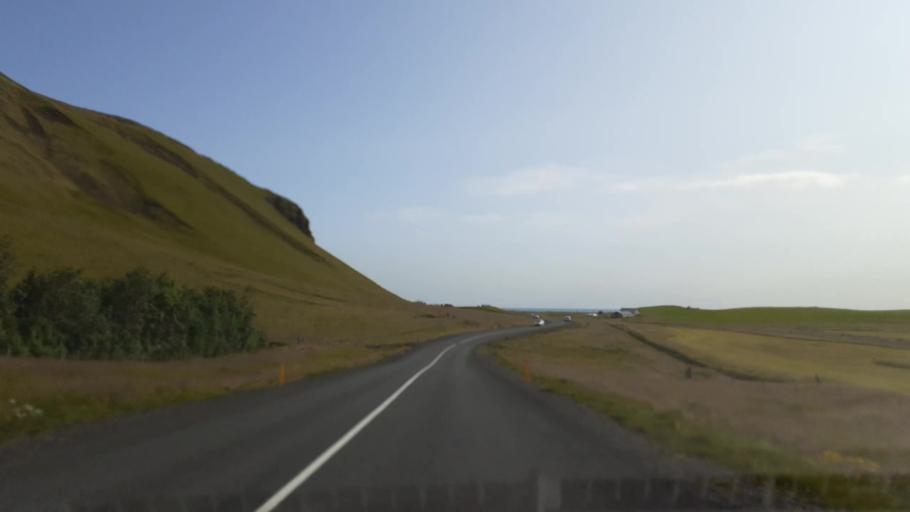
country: IS
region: South
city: Vestmannaeyjar
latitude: 63.4125
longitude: -19.0484
